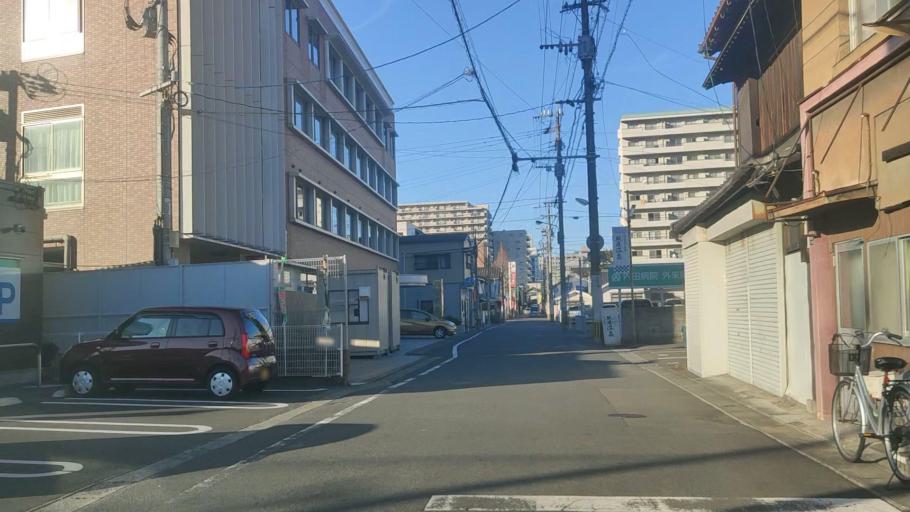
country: JP
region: Oita
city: Beppu
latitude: 33.2732
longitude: 131.5033
